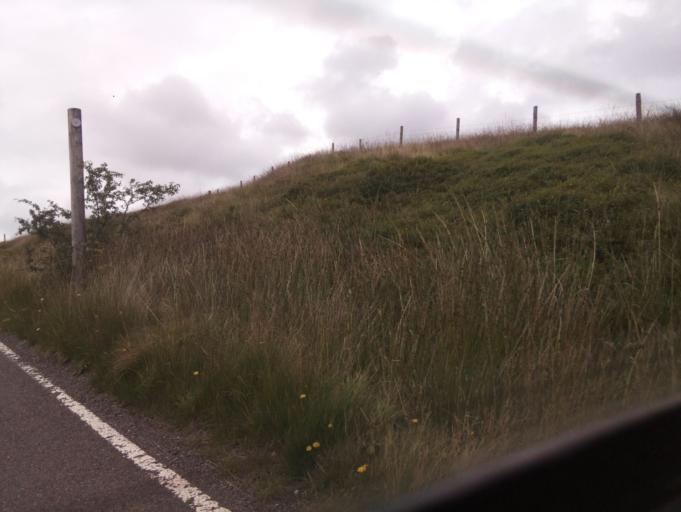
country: GB
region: England
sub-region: Kirklees
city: Meltham
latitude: 53.5130
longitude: -1.8528
